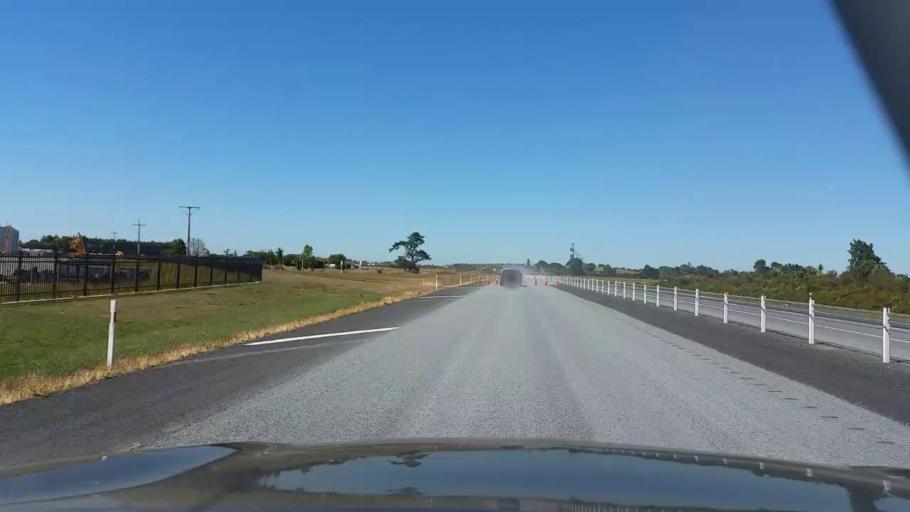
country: NZ
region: Waikato
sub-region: Hamilton City
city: Hamilton
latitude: -37.7412
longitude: 175.2132
